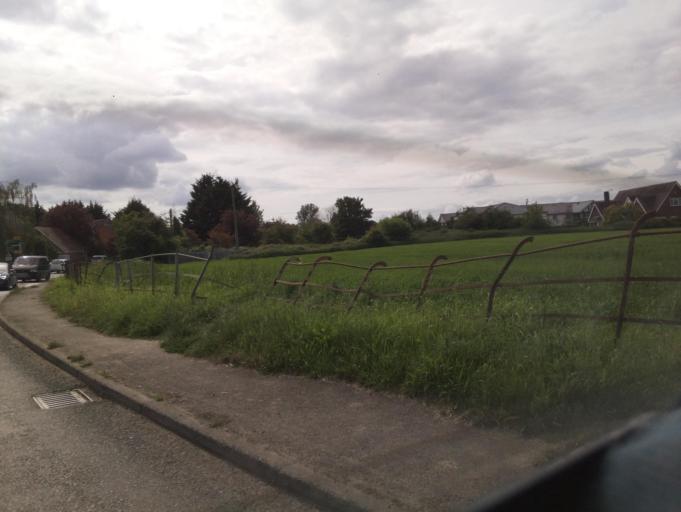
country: GB
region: England
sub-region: Worcestershire
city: Leigh
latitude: 52.1551
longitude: -2.3180
